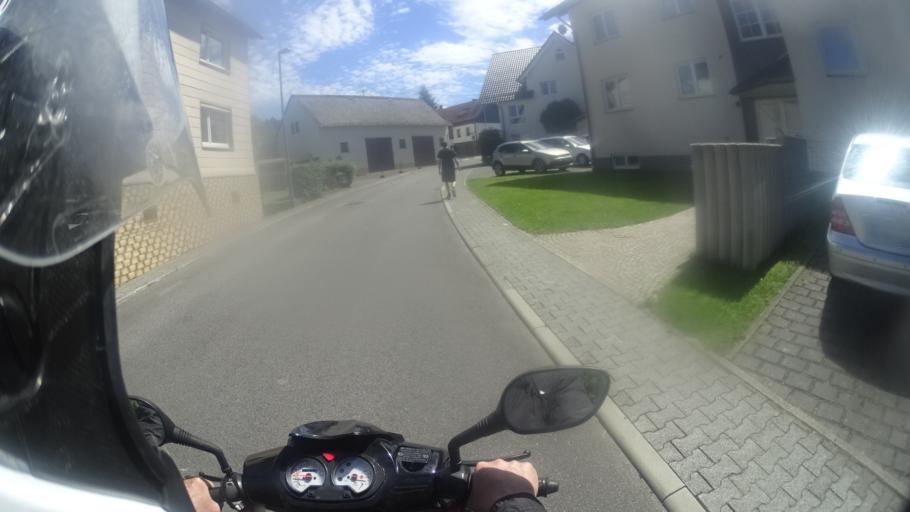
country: DE
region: Hesse
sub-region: Regierungsbezirk Darmstadt
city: Schlangenbad
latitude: 50.0844
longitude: 8.0441
